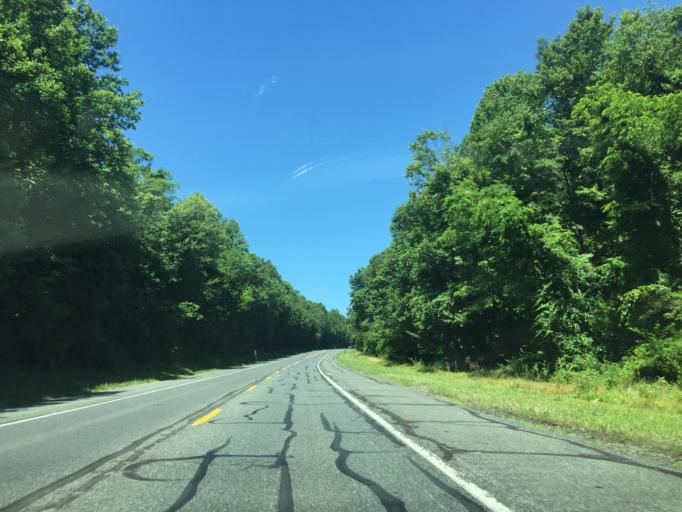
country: US
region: Maryland
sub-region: Harford County
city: Jarrettsville
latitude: 39.5770
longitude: -76.4412
